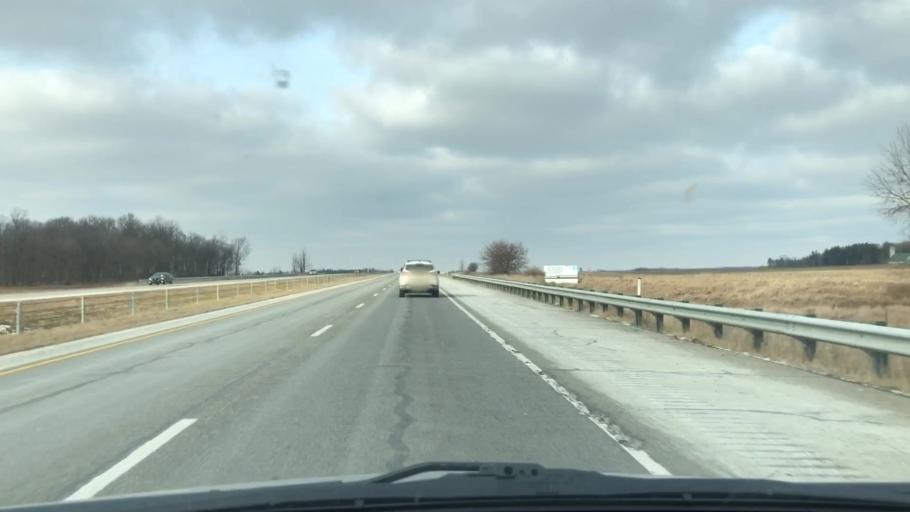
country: US
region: Indiana
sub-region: Steuben County
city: Angola
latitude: 41.5558
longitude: -85.0568
